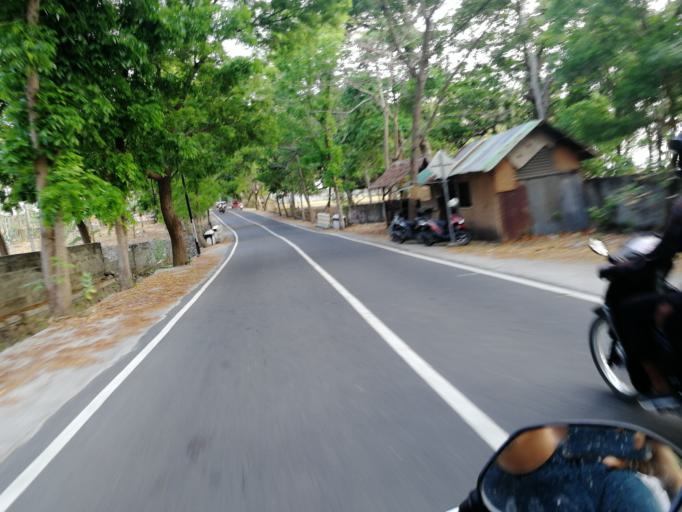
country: ID
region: West Nusa Tenggara
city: Karangsubagan
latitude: -8.4663
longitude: 116.0383
